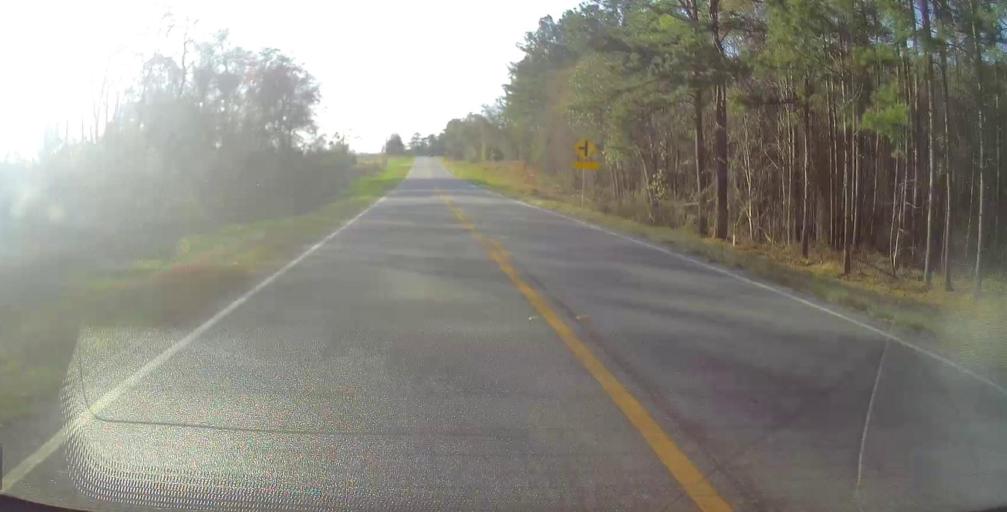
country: US
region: Georgia
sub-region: Toombs County
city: Lyons
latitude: 32.1431
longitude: -82.2517
